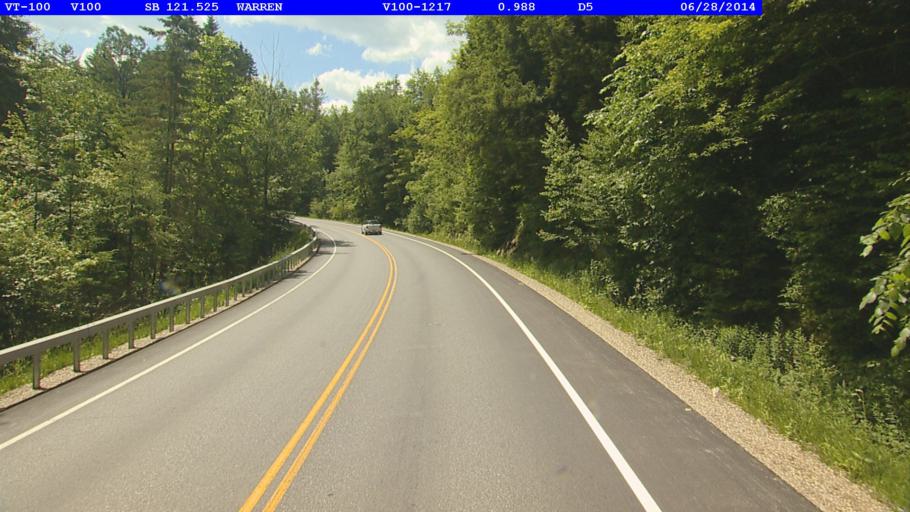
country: US
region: Vermont
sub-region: Washington County
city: Northfield
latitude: 44.0737
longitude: -72.8605
